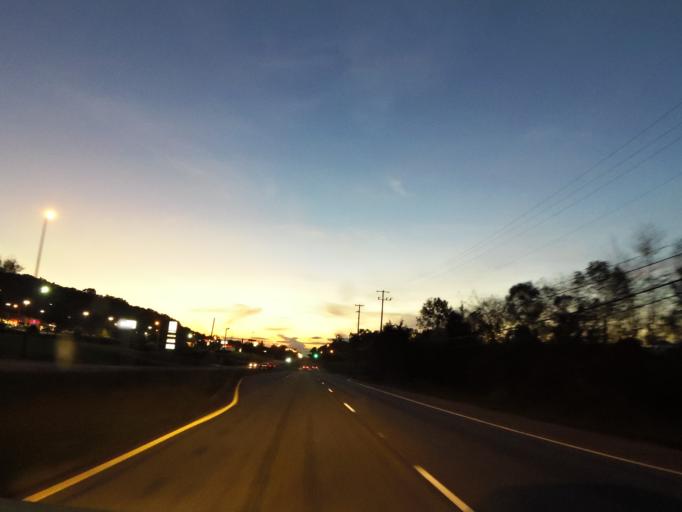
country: US
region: Tennessee
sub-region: Knox County
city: Mascot
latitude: 36.0218
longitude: -83.7749
